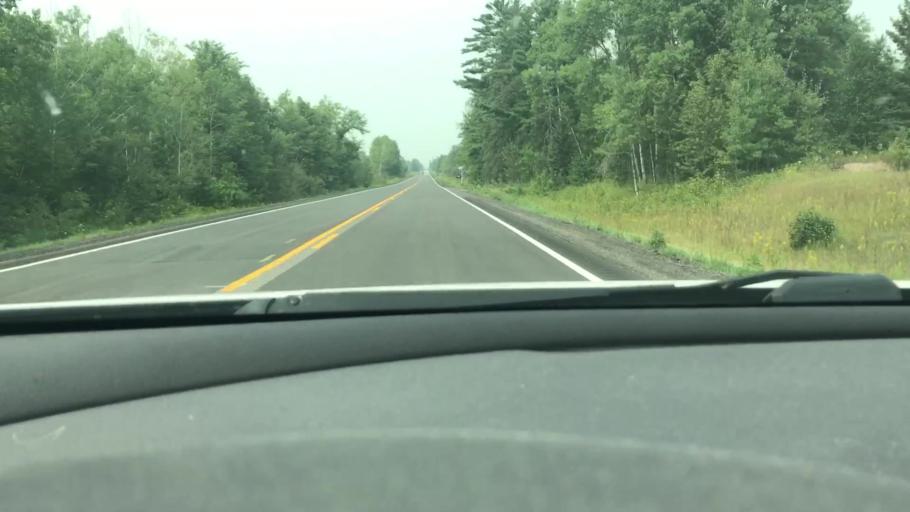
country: US
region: Minnesota
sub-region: Itasca County
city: Cohasset
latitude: 47.3603
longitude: -93.8624
